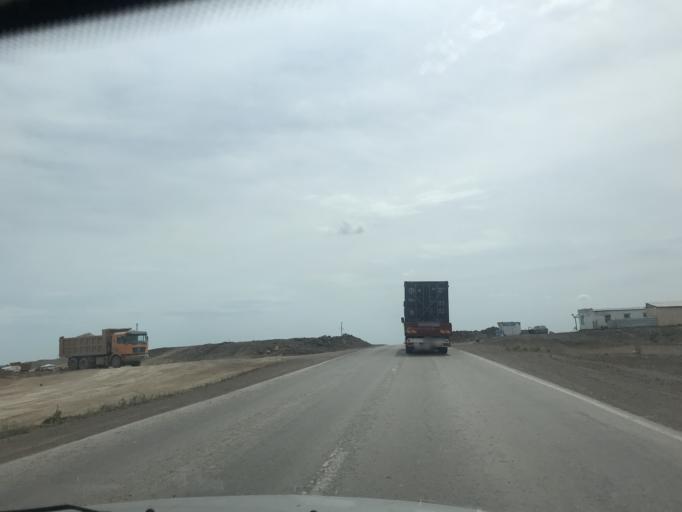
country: KZ
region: Zhambyl
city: Mynaral
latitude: 45.3445
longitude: 73.6972
